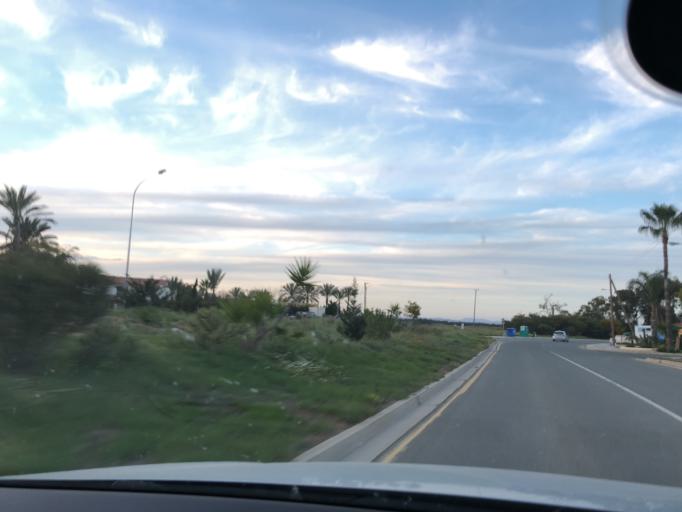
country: CY
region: Larnaka
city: Perivolia
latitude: 34.8355
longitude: 33.6046
